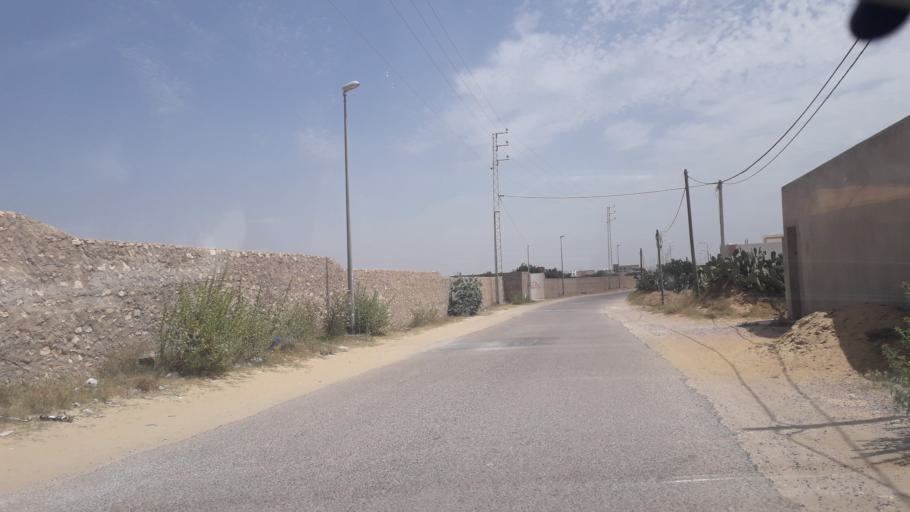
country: TN
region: Safaqis
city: Al Qarmadah
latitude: 34.8377
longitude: 10.7690
